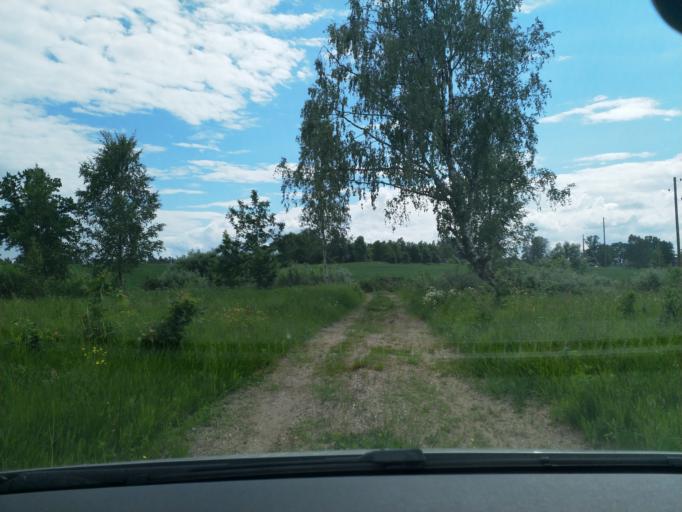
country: LV
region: Kuldigas Rajons
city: Kuldiga
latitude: 56.8380
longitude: 21.9380
